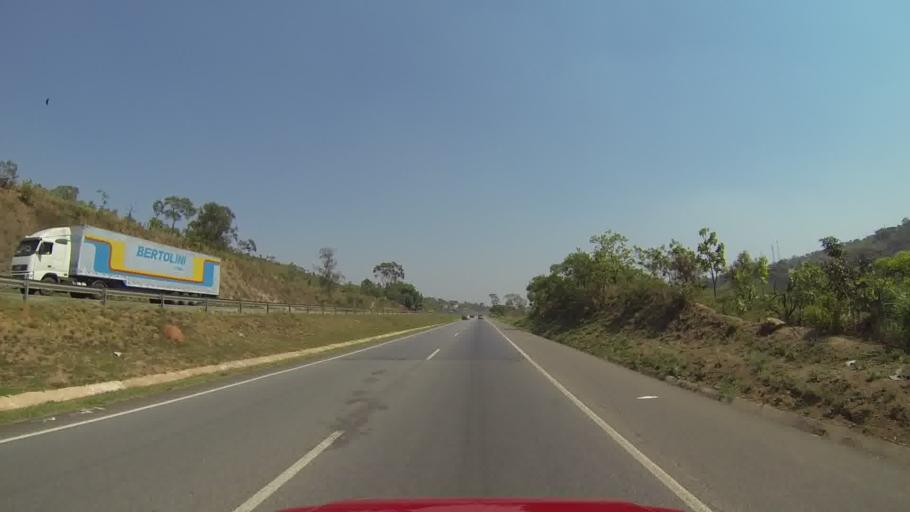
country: BR
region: Minas Gerais
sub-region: Belo Horizonte
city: Belo Horizonte
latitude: -19.9231
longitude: -43.9433
